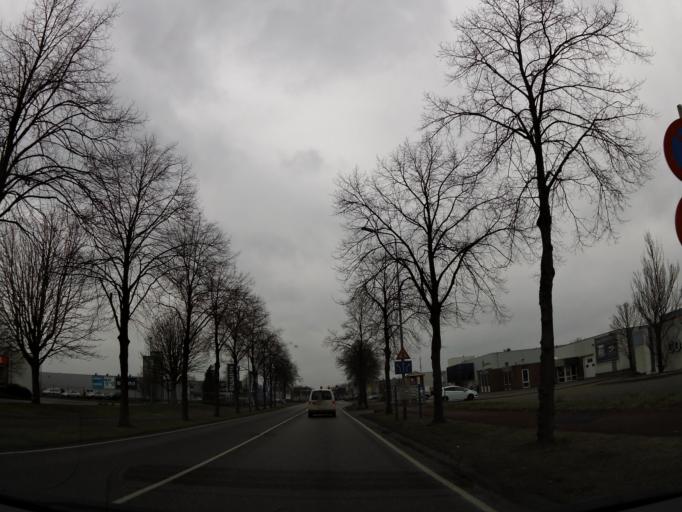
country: NL
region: Limburg
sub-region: Gemeente Sittard-Geleen
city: Sittard
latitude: 51.0191
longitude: 5.8684
